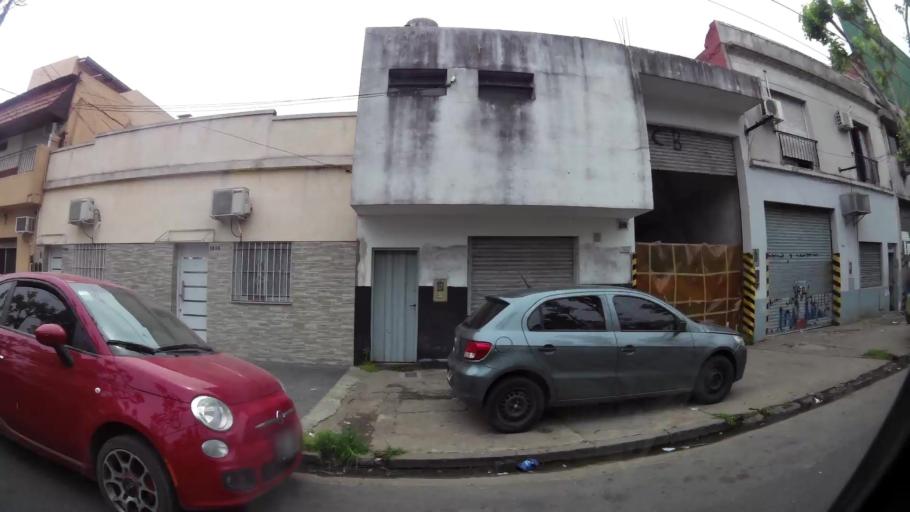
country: AR
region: Buenos Aires
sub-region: Partido de Avellaneda
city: Avellaneda
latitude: -34.6658
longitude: -58.3489
